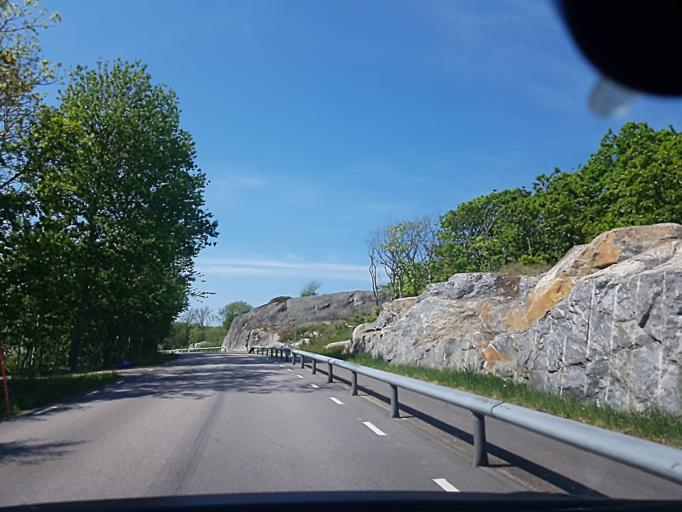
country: SE
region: Vaestra Goetaland
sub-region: Lysekils Kommun
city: Lysekil
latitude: 58.1683
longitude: 11.4327
